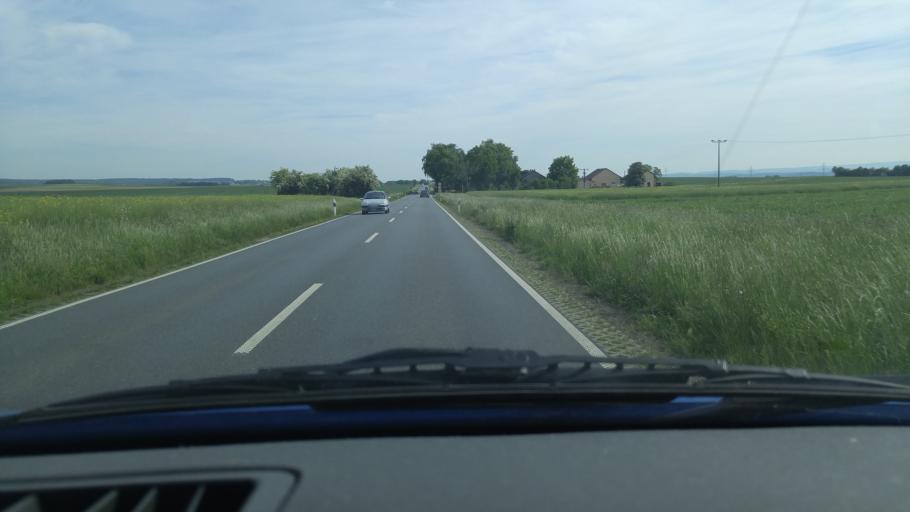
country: DE
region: Hesse
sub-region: Regierungsbezirk Darmstadt
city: Wolfersheim
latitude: 50.3623
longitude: 8.7956
